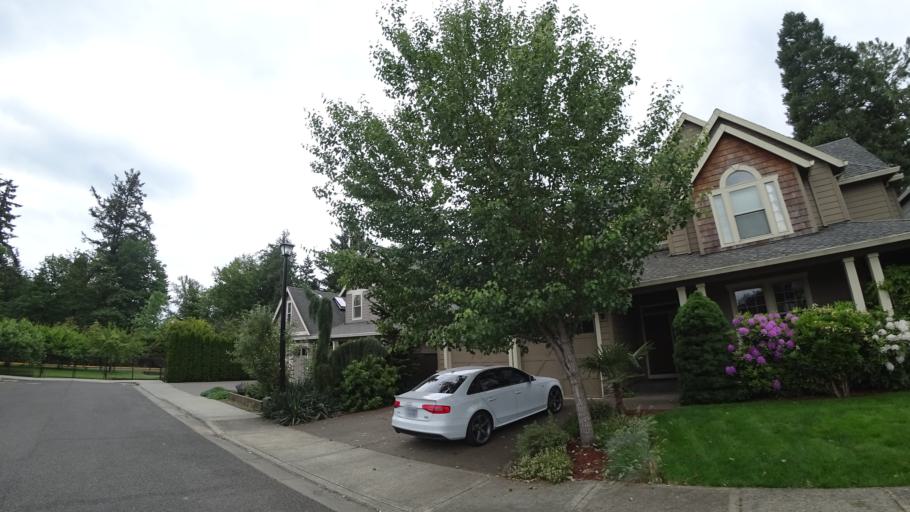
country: US
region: Oregon
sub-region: Washington County
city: West Slope
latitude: 45.4900
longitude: -122.7793
